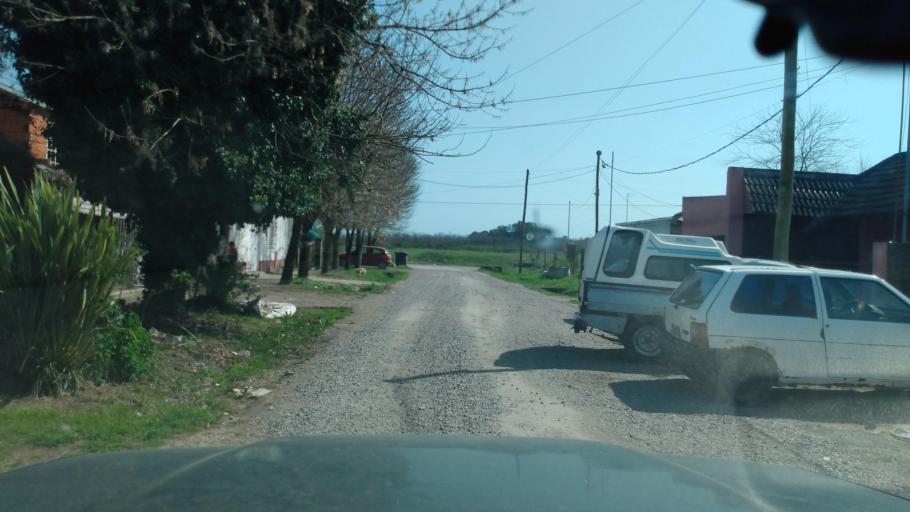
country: AR
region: Buenos Aires
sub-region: Partido de Lujan
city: Lujan
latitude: -34.5465
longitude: -59.1062
